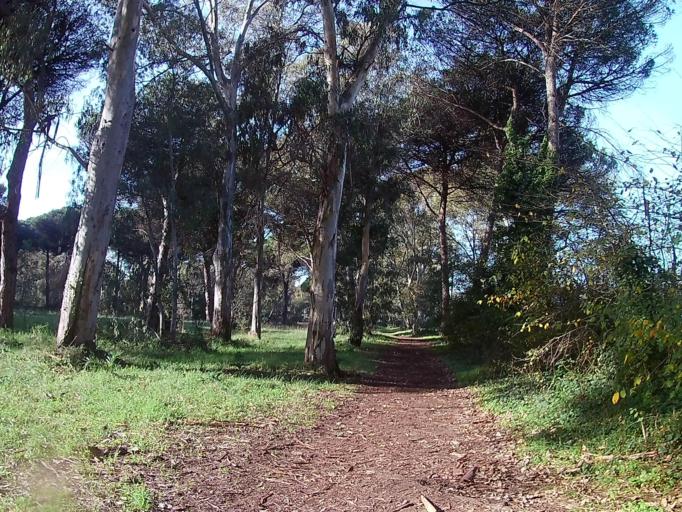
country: IT
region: Latium
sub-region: Citta metropolitana di Roma Capitale
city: Lido di Ostia
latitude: 41.7465
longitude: 12.2781
